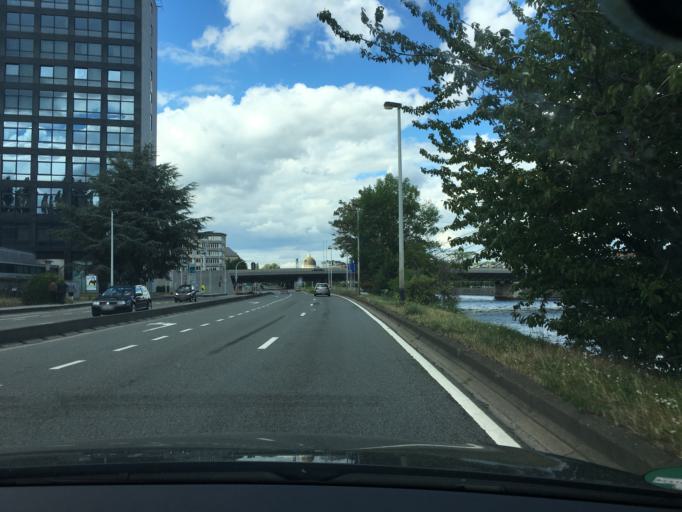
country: BE
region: Wallonia
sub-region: Province de Liege
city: Liege
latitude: 50.6149
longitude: 5.5768
